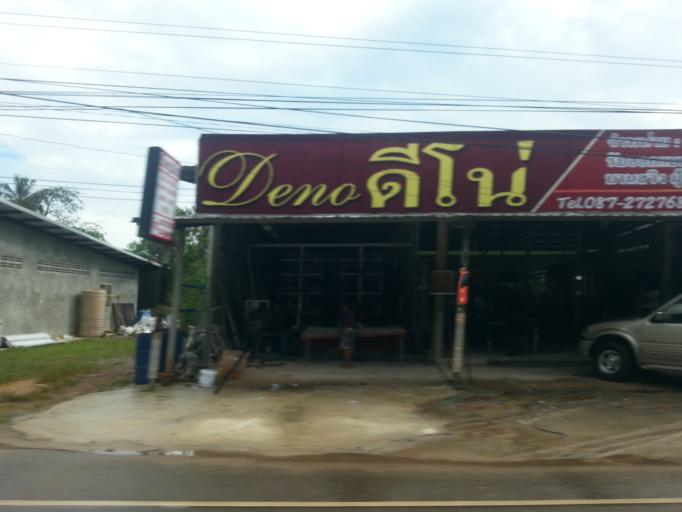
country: TH
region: Krabi
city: Krabi
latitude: 8.0805
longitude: 98.8707
